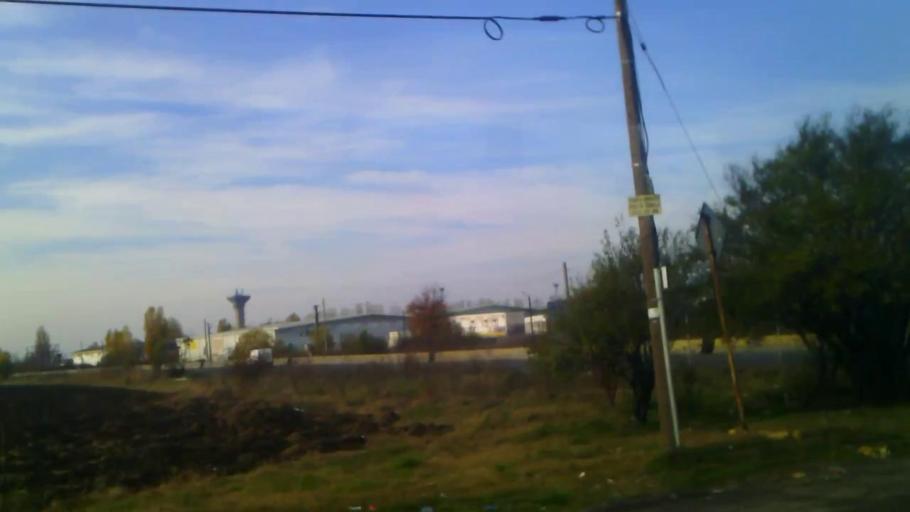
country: RO
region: Ilfov
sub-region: Comuna Berceni
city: Berceni
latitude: 44.3399
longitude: 26.1654
